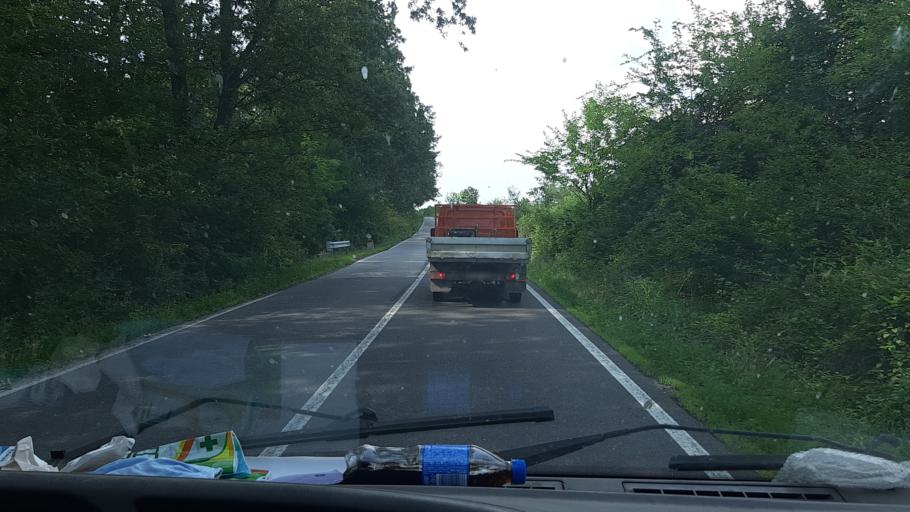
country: RO
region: Caras-Severin
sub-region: Comuna Farliug
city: Farliug
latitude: 45.5411
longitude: 21.8769
